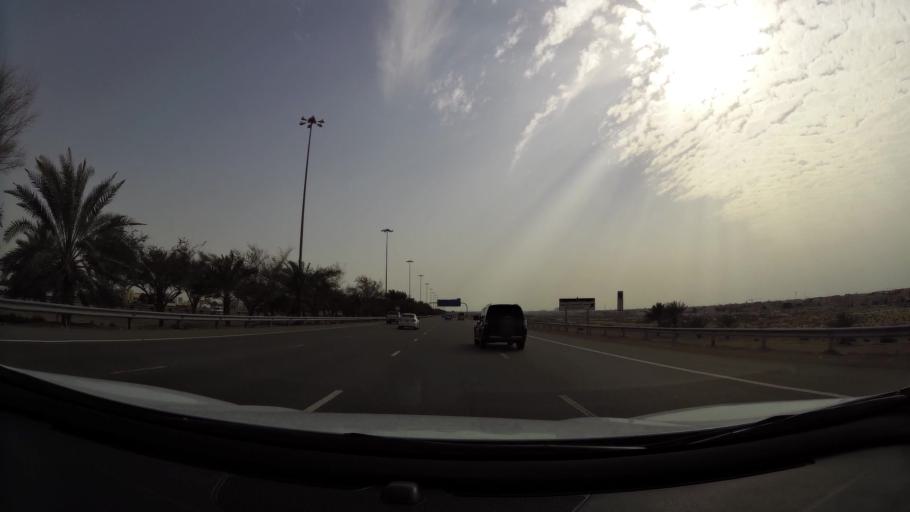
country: AE
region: Abu Dhabi
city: Abu Dhabi
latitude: 24.3816
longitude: 54.6600
